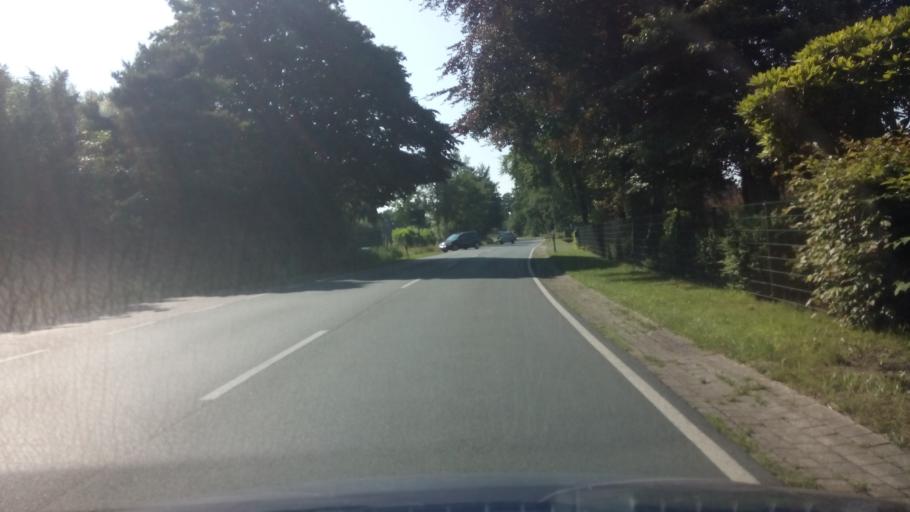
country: DE
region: Lower Saxony
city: Grasberg
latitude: 53.1351
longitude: 8.9811
